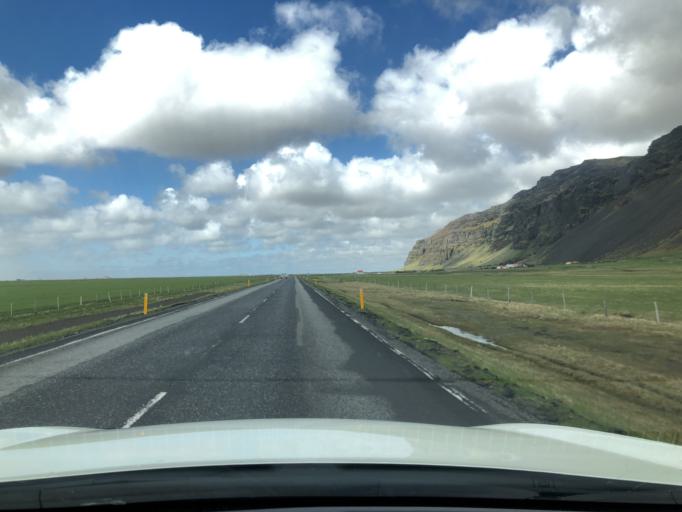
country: IS
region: South
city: Vestmannaeyjar
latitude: 63.5795
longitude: -19.9082
